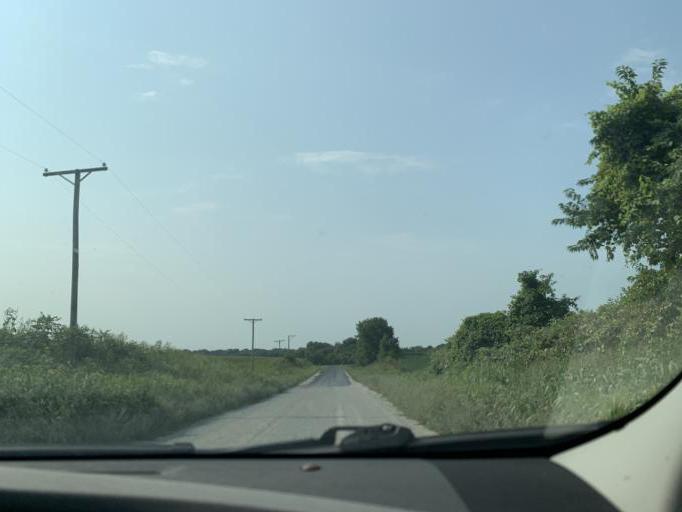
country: US
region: Illinois
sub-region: Whiteside County
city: Sterling
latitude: 41.8261
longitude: -89.7472
